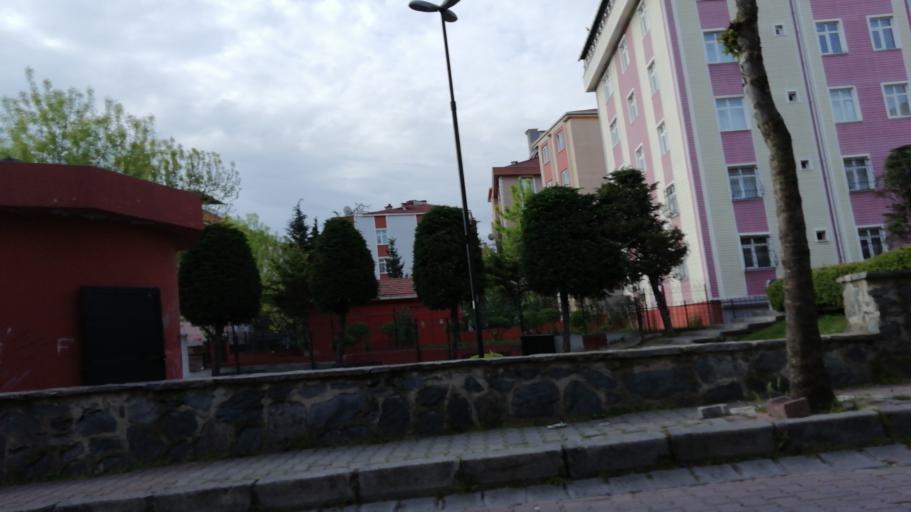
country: TR
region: Istanbul
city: Bagcilar
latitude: 41.0210
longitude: 28.8355
